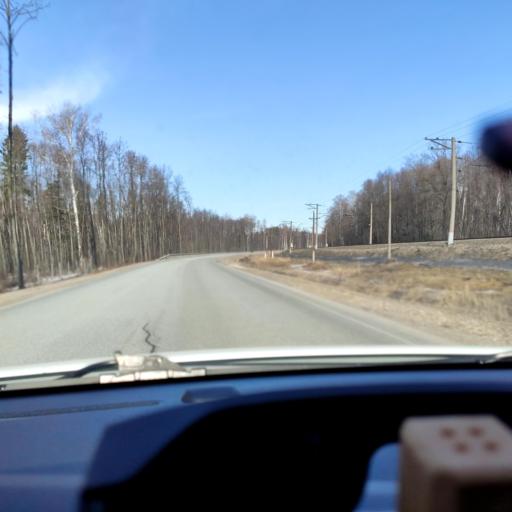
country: RU
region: Tatarstan
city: Vysokaya Gora
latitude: 55.9188
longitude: 49.2819
